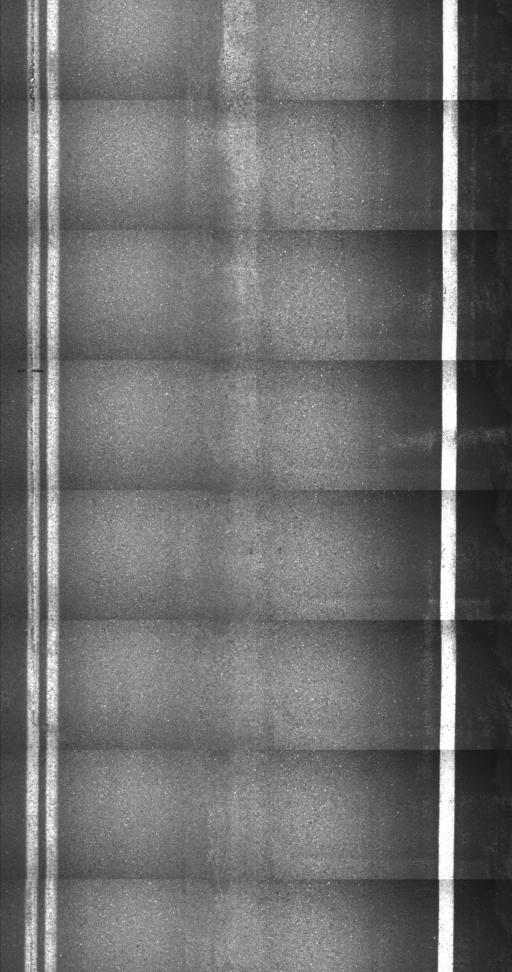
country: US
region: Vermont
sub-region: Caledonia County
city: Lyndonville
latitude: 44.6427
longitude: -72.1548
